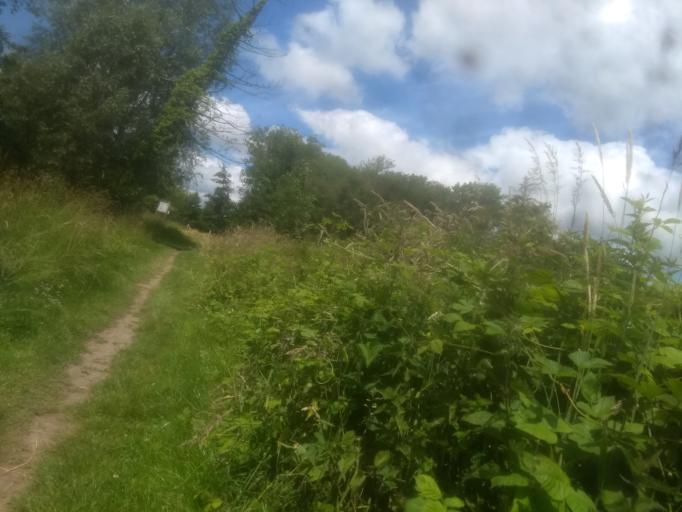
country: FR
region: Nord-Pas-de-Calais
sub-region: Departement du Pas-de-Calais
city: Maroeuil
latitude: 50.3169
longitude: 2.7074
